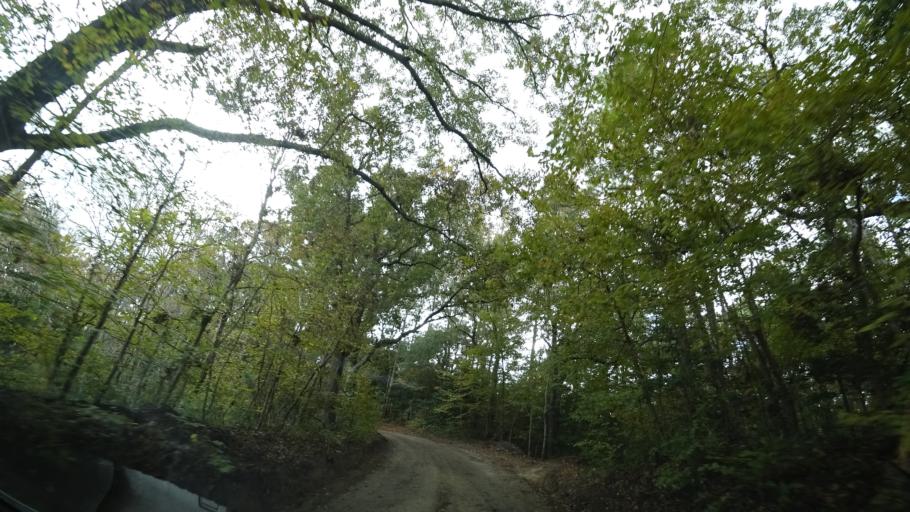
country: US
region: North Carolina
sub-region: Dare County
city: Kill Devil Hills
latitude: 35.9964
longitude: -75.6662
